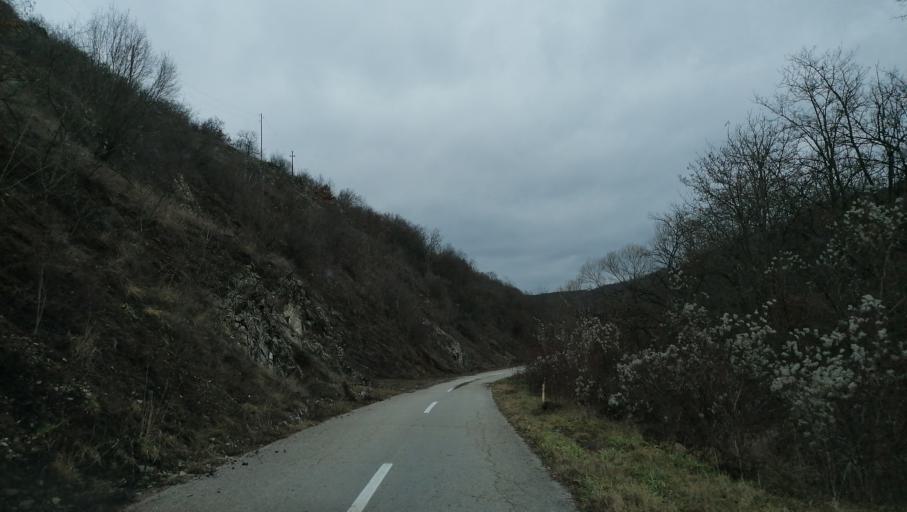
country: RS
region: Central Serbia
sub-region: Pirotski Okrug
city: Dimitrovgrad
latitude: 42.9494
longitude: 22.7694
